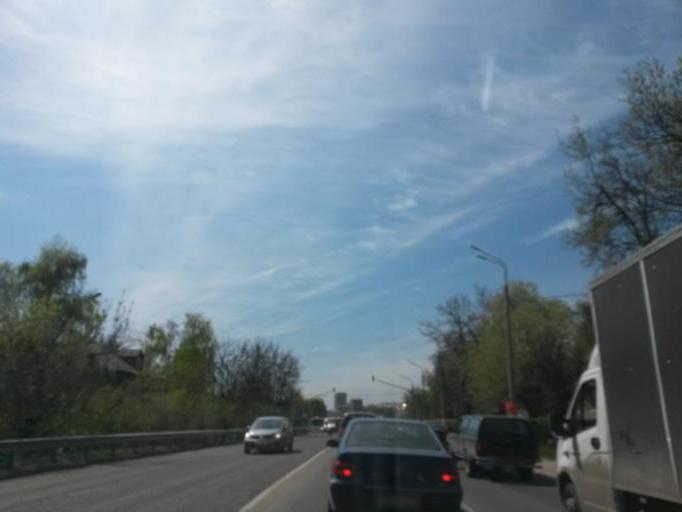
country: RU
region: Moskovskaya
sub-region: Podol'skiy Rayon
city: Podol'sk
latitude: 55.4384
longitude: 37.5563
